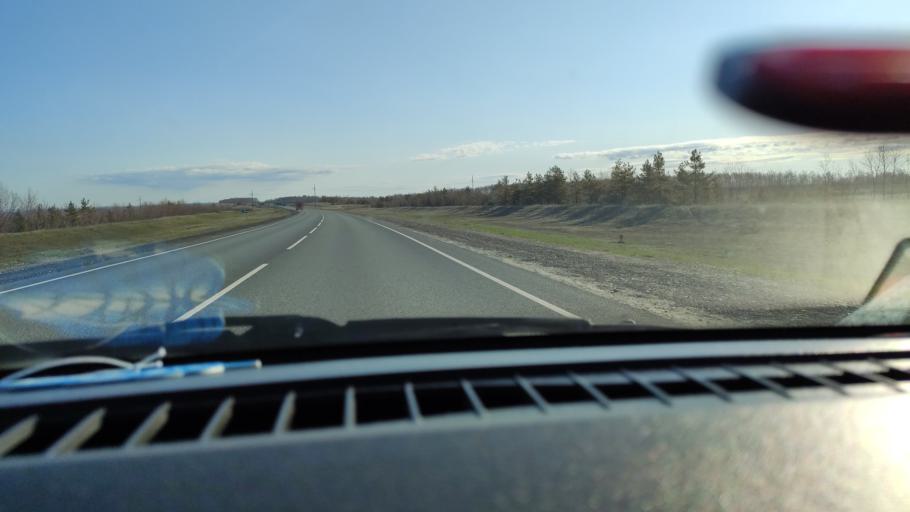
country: RU
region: Saratov
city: Khvalynsk
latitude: 52.5451
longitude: 48.0662
